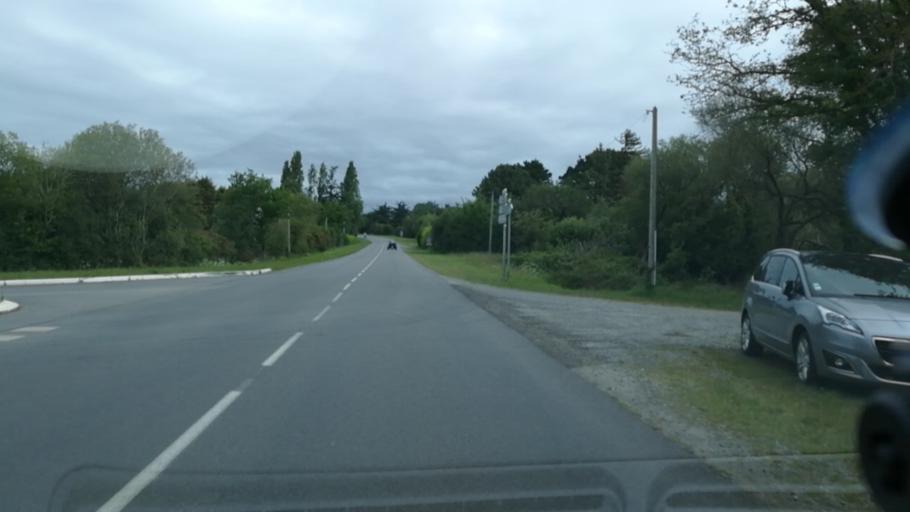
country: FR
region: Brittany
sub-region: Departement du Morbihan
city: Penestin
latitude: 47.4696
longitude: -2.4789
